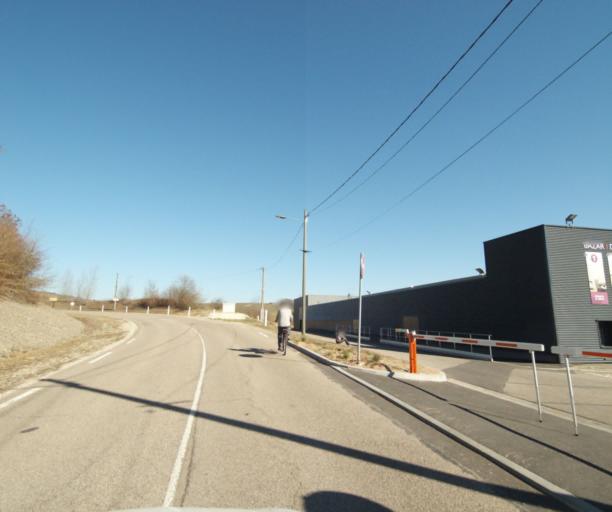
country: FR
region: Lorraine
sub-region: Departement de Meurthe-et-Moselle
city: Essey-les-Nancy
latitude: 48.7129
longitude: 6.2405
